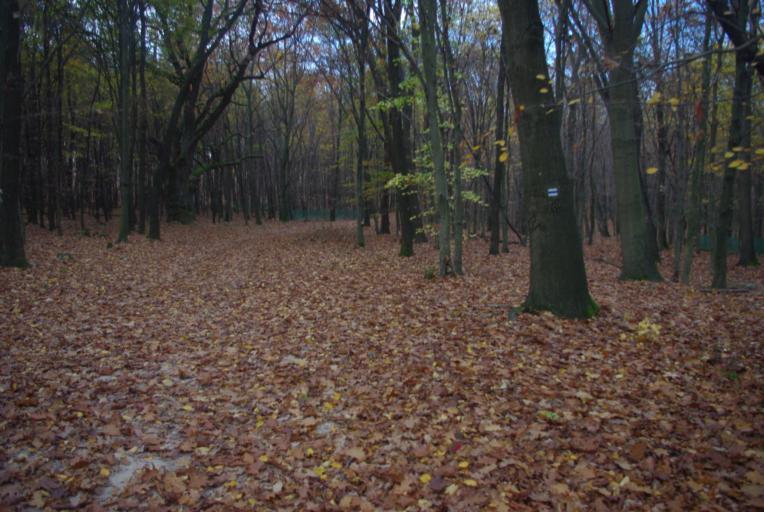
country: HU
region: Borsod-Abauj-Zemplen
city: Sarospatak
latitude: 48.3903
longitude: 21.5668
